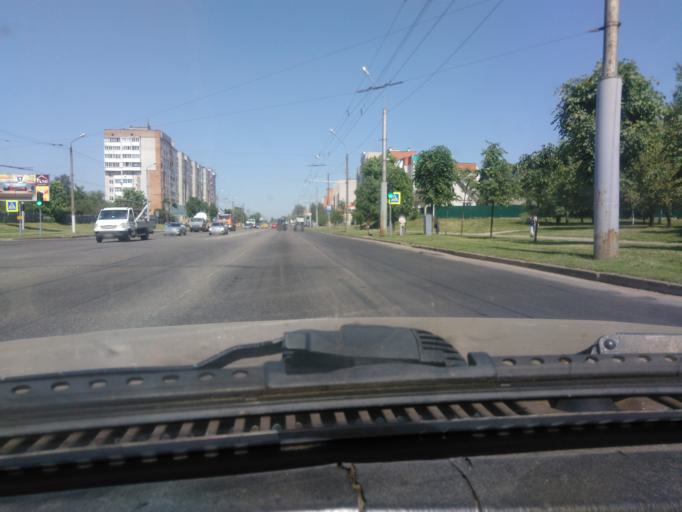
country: BY
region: Mogilev
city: Mahilyow
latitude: 53.9313
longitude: 30.3518
